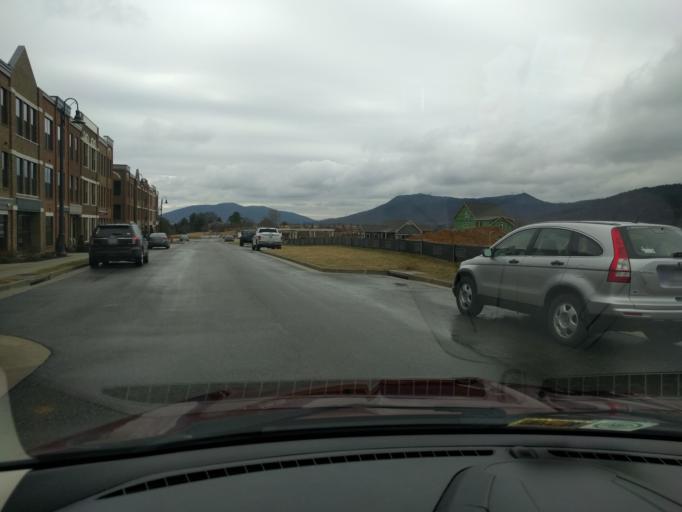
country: US
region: Virginia
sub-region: Botetourt County
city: Daleville
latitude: 37.4165
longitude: -79.9151
